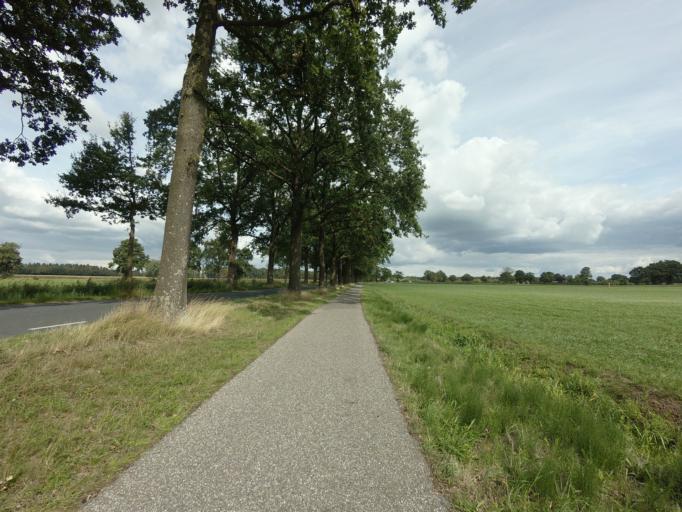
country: NL
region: Overijssel
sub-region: Gemeente Deventer
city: Schalkhaar
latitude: 52.2772
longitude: 6.2088
